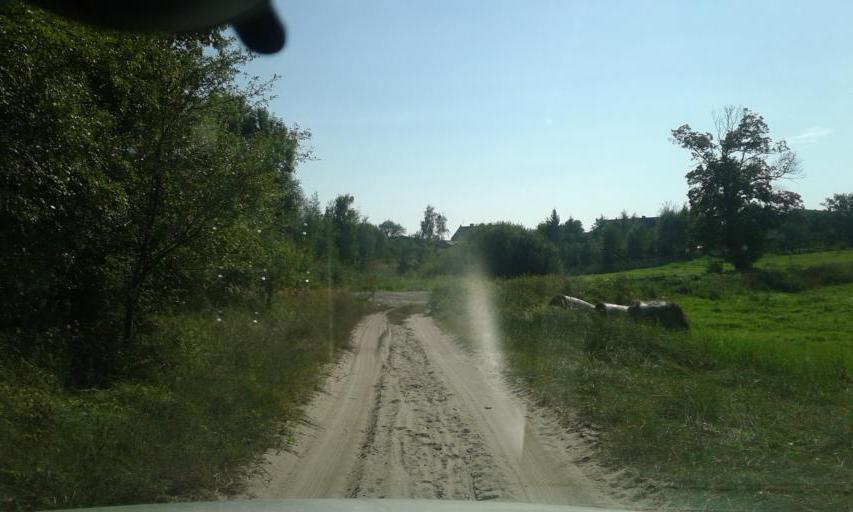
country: PL
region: West Pomeranian Voivodeship
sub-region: Powiat choszczenski
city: Krzecin
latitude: 53.0848
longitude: 15.4894
